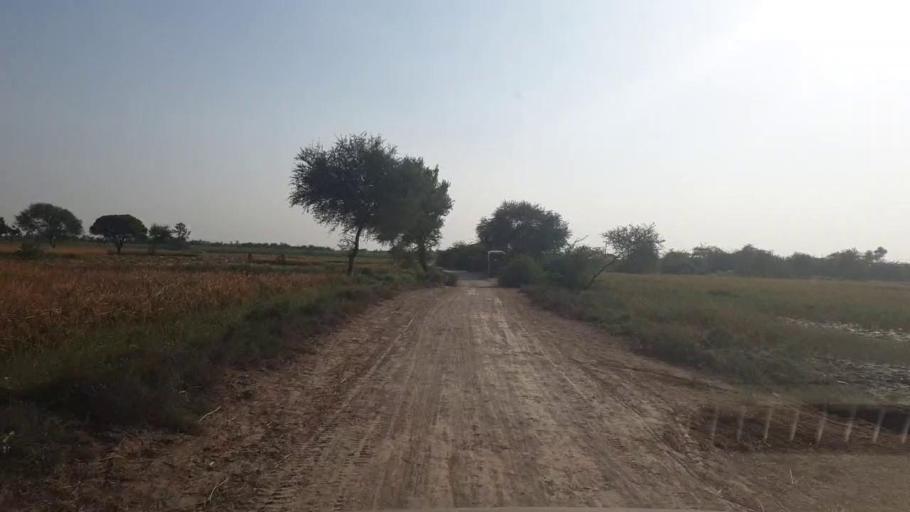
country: PK
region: Sindh
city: Badin
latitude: 24.6351
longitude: 68.7984
